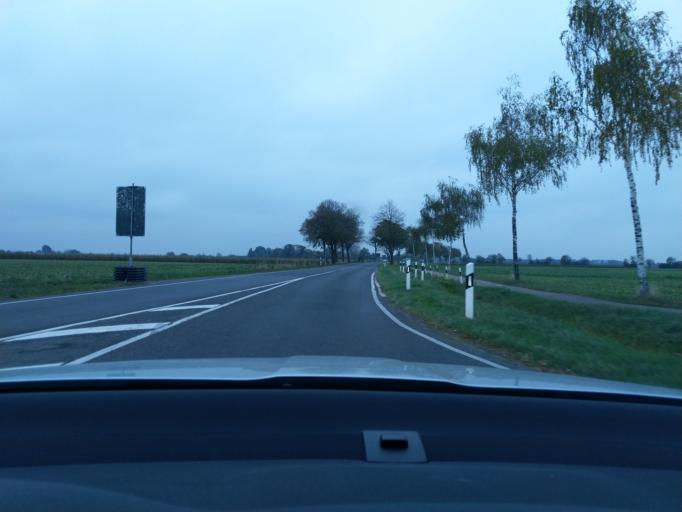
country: DE
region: North Rhine-Westphalia
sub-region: Regierungsbezirk Dusseldorf
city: Schwalmtal
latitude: 51.2272
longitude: 6.2958
